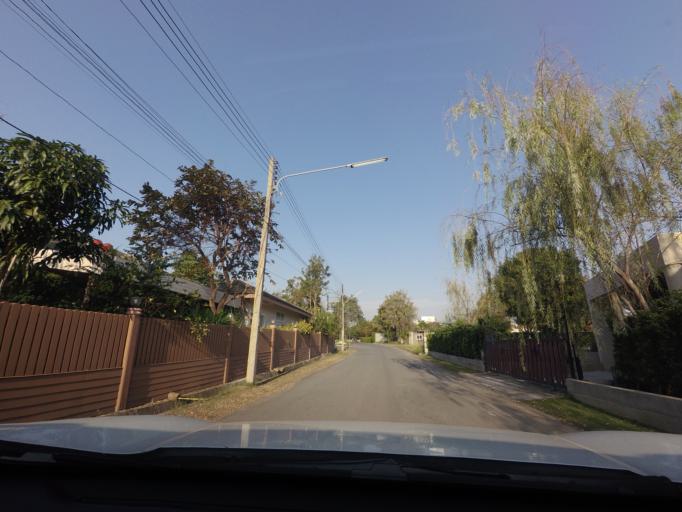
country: TH
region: Nakhon Ratchasima
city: Pak Chong
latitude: 14.5860
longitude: 101.4487
